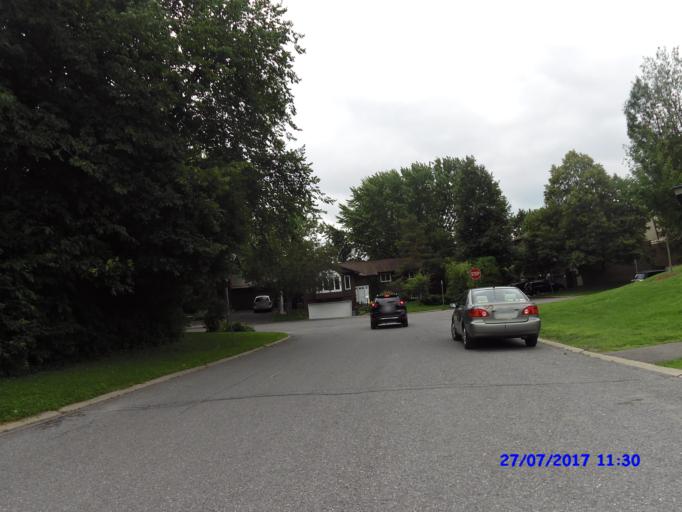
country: CA
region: Ontario
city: Ottawa
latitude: 45.3629
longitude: -75.7281
